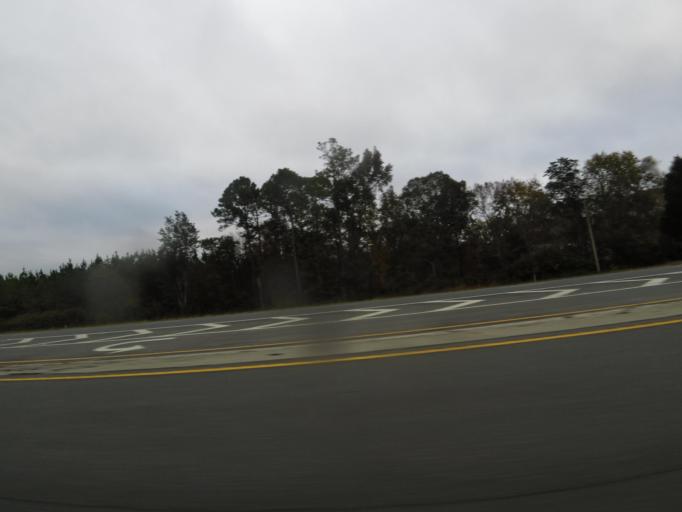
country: US
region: Georgia
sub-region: Charlton County
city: Folkston
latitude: 30.9115
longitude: -82.0771
